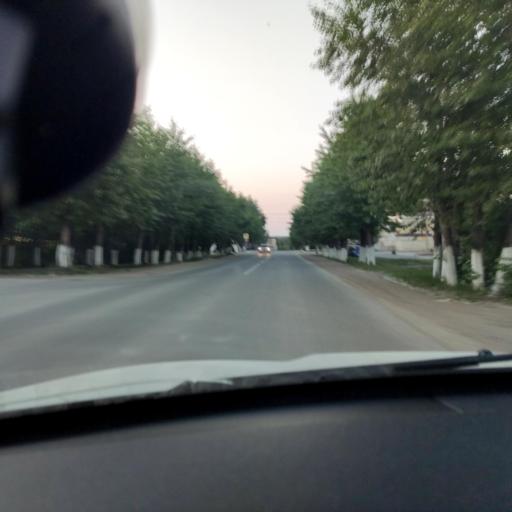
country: RU
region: Perm
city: Polazna
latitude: 58.2939
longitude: 56.4022
